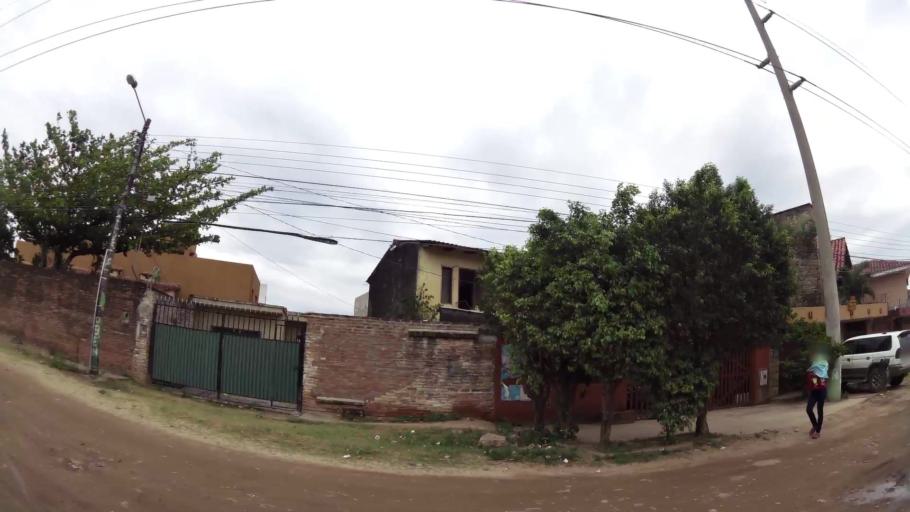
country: BO
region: Santa Cruz
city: Santa Cruz de la Sierra
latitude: -17.7482
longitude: -63.1849
